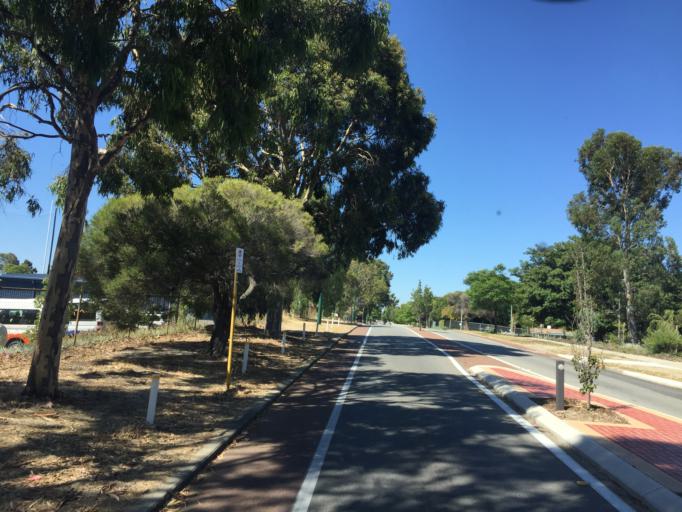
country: AU
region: Western Australia
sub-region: Victoria Park
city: Victoria Park
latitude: -31.9743
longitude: 115.9088
